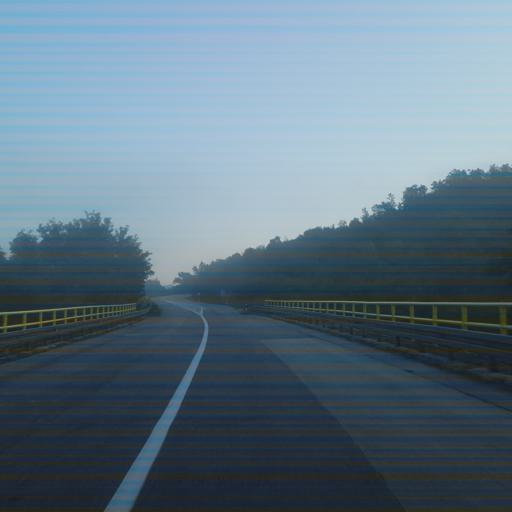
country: RS
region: Central Serbia
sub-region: Zajecarski Okrug
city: Zajecar
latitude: 43.9832
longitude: 22.2947
